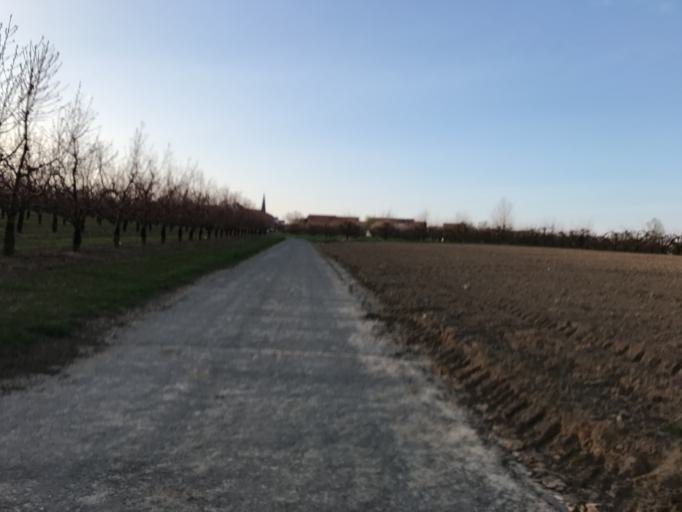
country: DE
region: Rheinland-Pfalz
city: Ober-Olm
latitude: 49.9703
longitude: 8.1929
